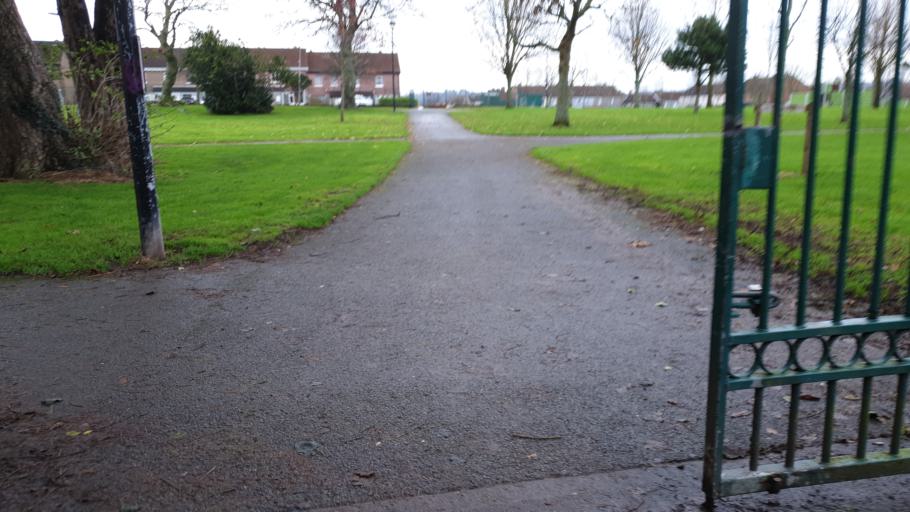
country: IE
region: Munster
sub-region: County Cork
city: Passage West
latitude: 51.8920
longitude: -8.3998
